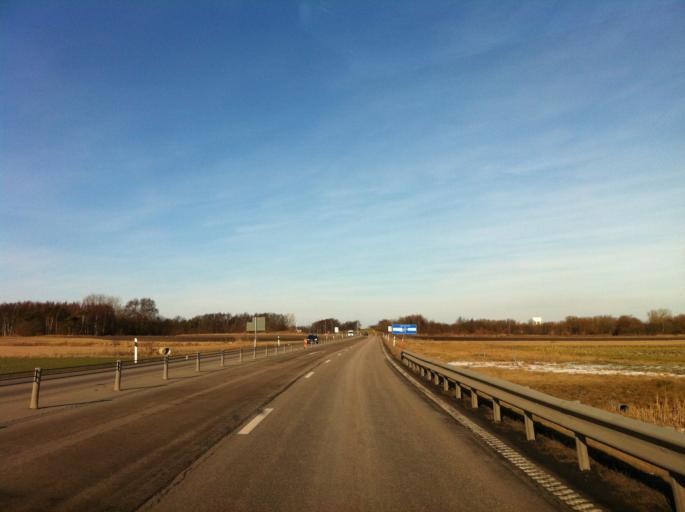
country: SE
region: Skane
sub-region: Helsingborg
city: Odakra
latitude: 56.1096
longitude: 12.6927
